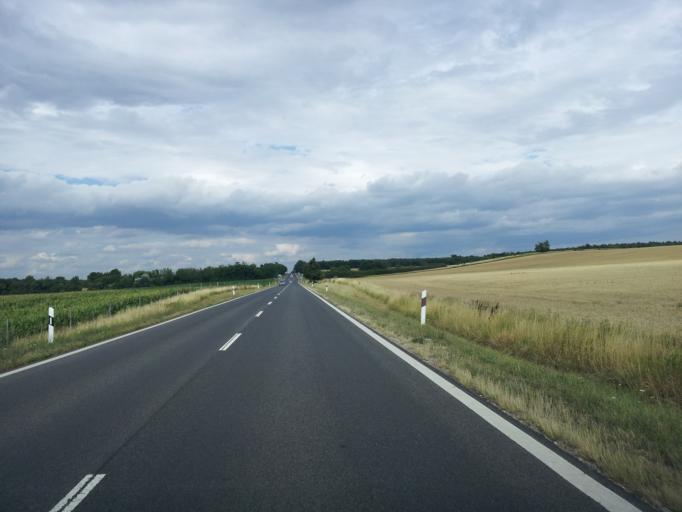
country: HU
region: Vas
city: Janoshaza
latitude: 47.0965
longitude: 17.0617
